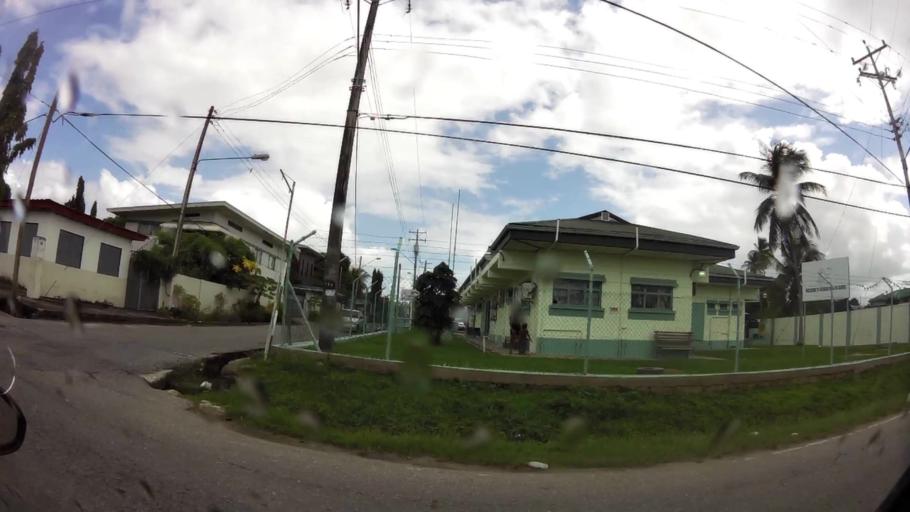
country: TT
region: Tunapuna/Piarco
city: Arouca
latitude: 10.6291
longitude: -61.3389
